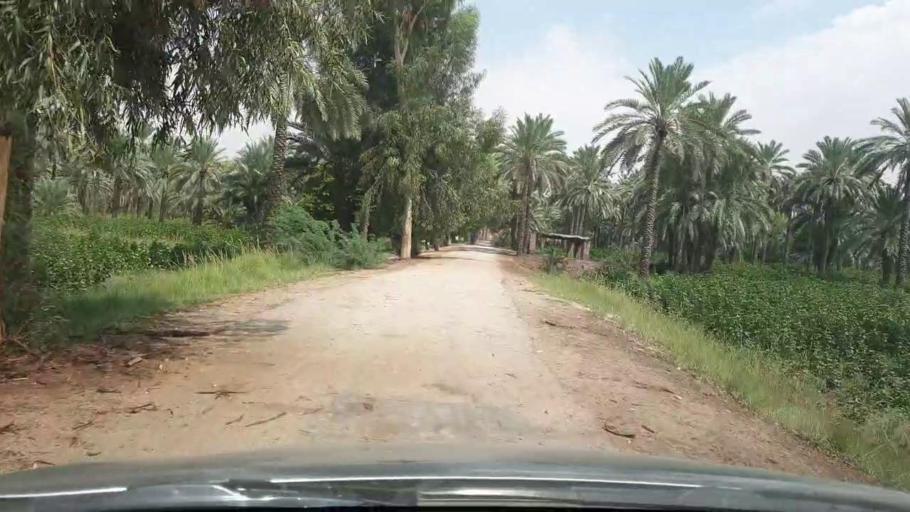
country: PK
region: Sindh
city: Kot Diji
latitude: 27.3945
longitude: 68.7418
